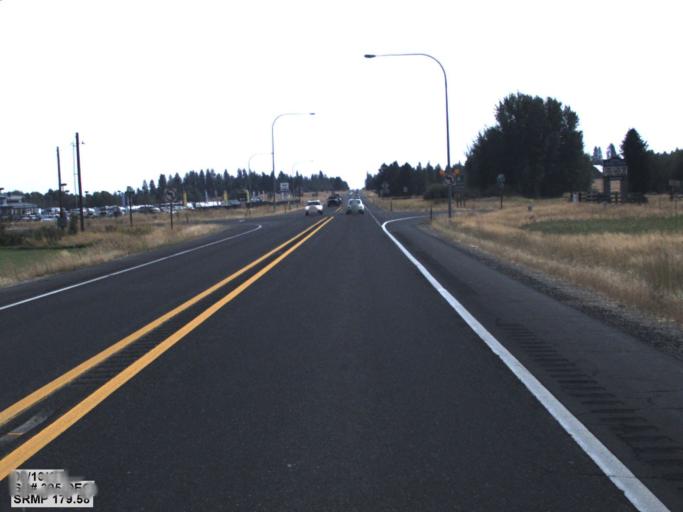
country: US
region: Washington
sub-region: Spokane County
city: Deer Park
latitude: 47.9433
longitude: -117.4779
